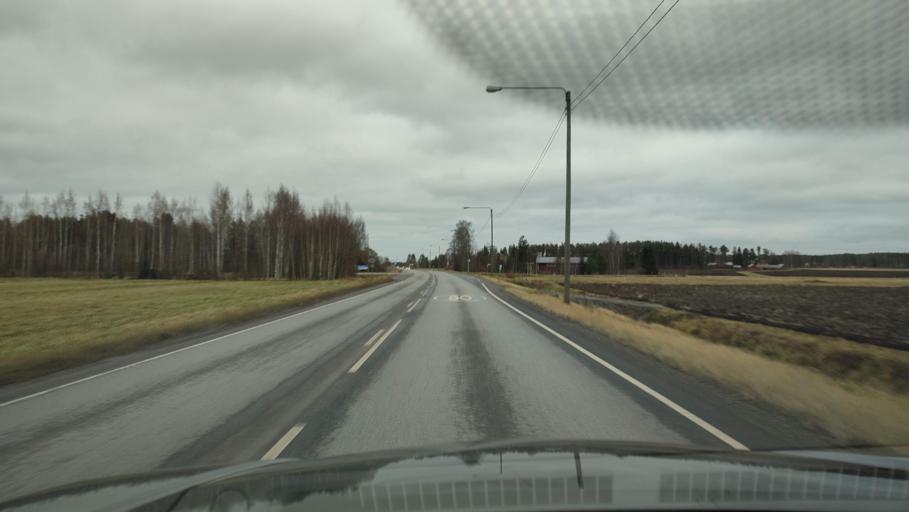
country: FI
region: Southern Ostrobothnia
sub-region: Seinaejoki
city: Kurikka
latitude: 62.6815
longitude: 22.4795
